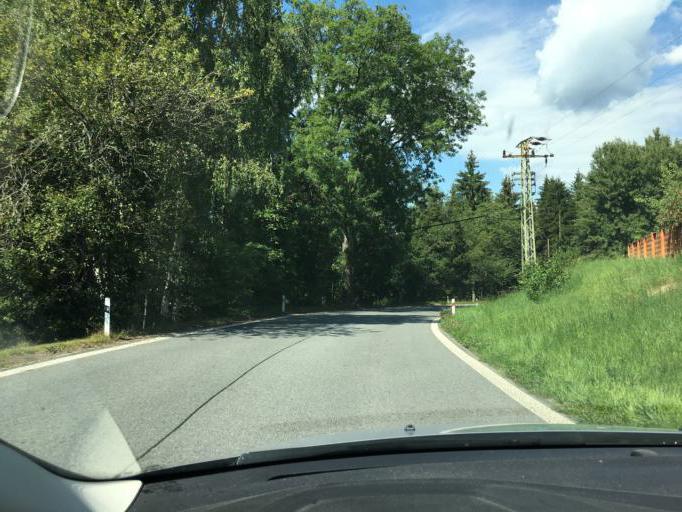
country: CZ
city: Plavy
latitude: 50.7024
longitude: 15.3436
